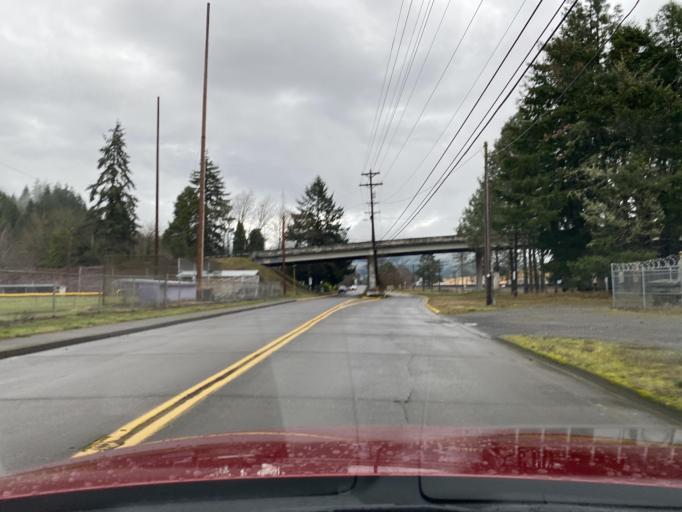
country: US
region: Oregon
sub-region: Lane County
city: Oakridge
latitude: 43.7472
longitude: -122.4682
